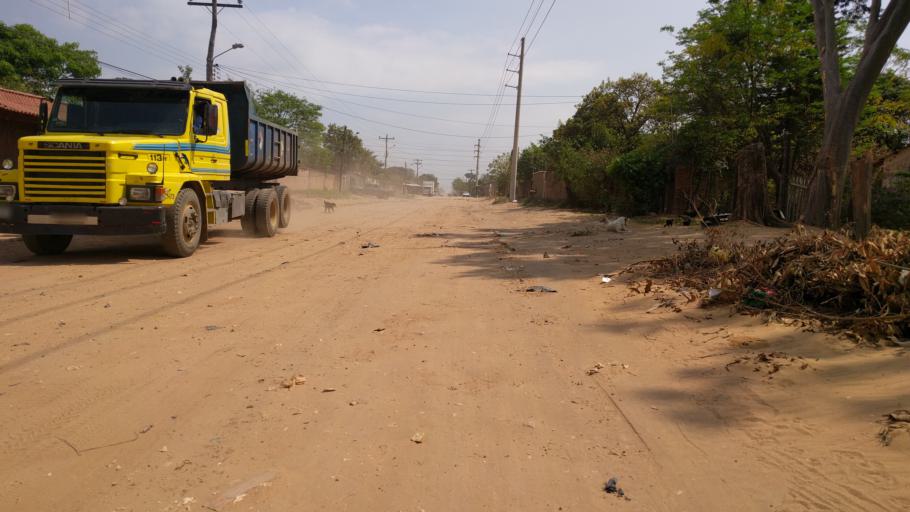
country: BO
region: Santa Cruz
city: Santa Cruz de la Sierra
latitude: -17.8526
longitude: -63.2178
